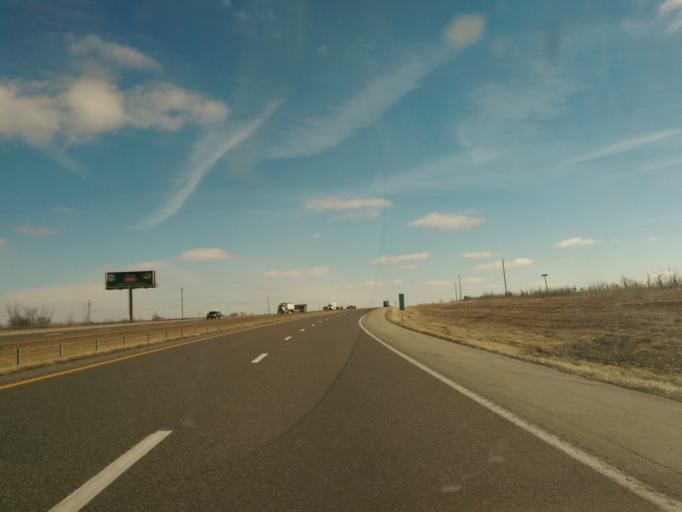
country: US
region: Missouri
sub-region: Callaway County
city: Fulton
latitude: 38.9434
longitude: -91.8800
